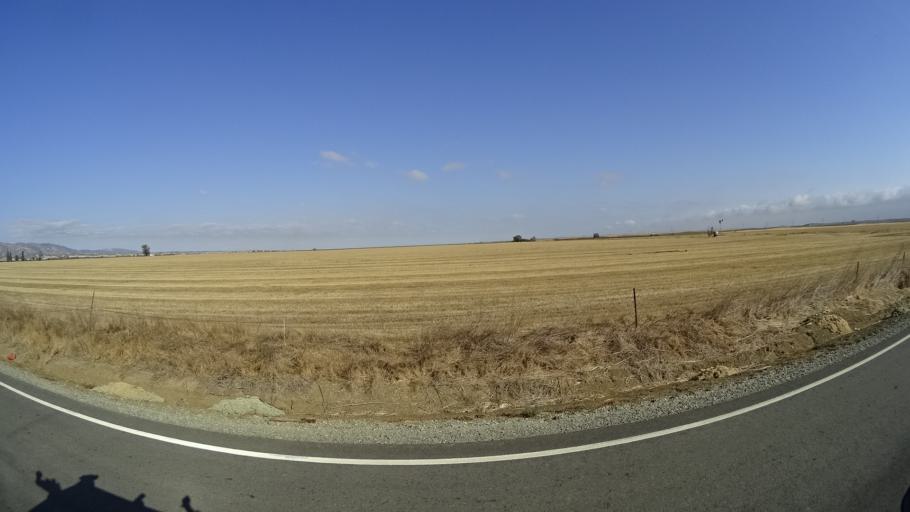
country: US
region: California
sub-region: Yolo County
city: Esparto
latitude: 38.7811
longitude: -122.0366
